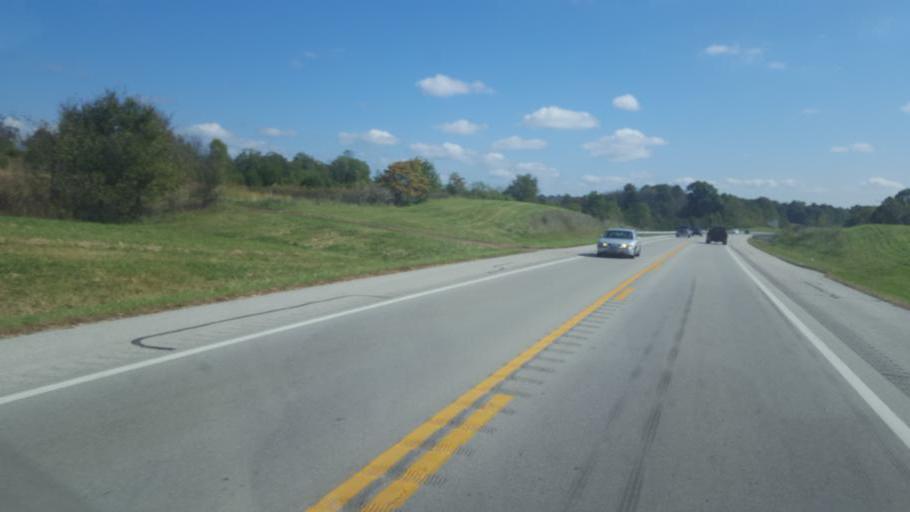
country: US
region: Kentucky
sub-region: Mason County
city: Maysville
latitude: 38.5824
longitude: -83.6792
